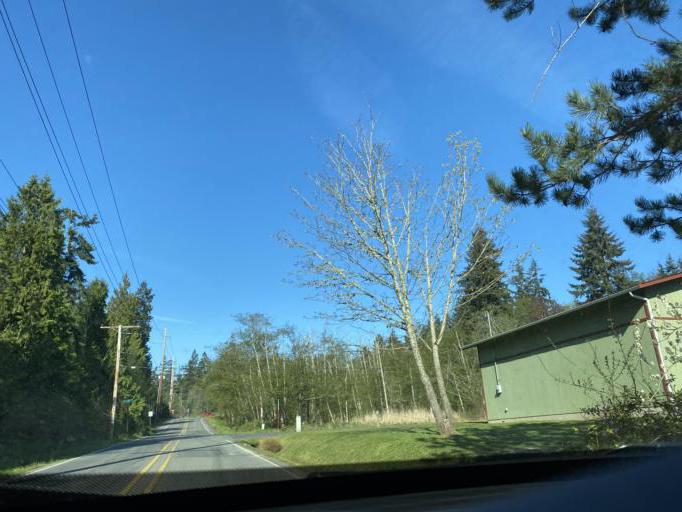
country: US
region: Washington
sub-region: Island County
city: Freeland
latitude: 48.0155
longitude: -122.5424
